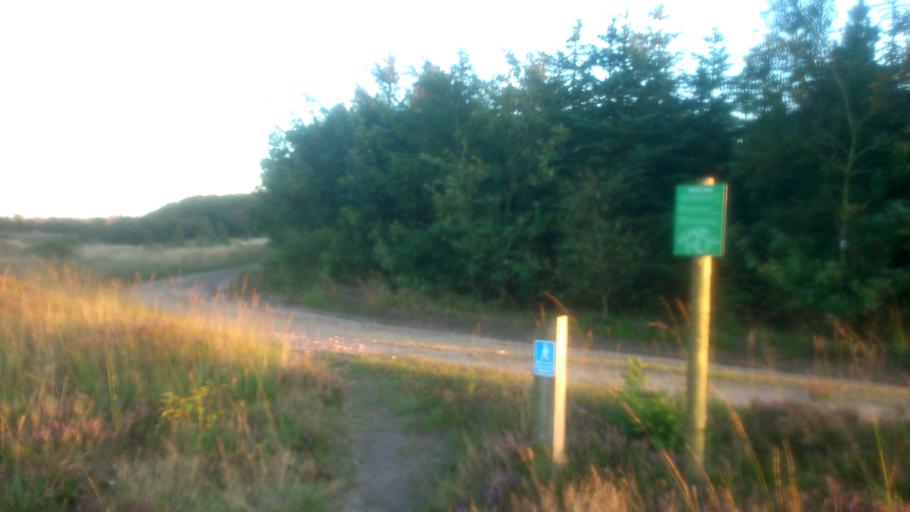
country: DK
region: Central Jutland
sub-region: Ringkobing-Skjern Kommune
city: Skjern
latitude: 56.0231
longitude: 8.4614
